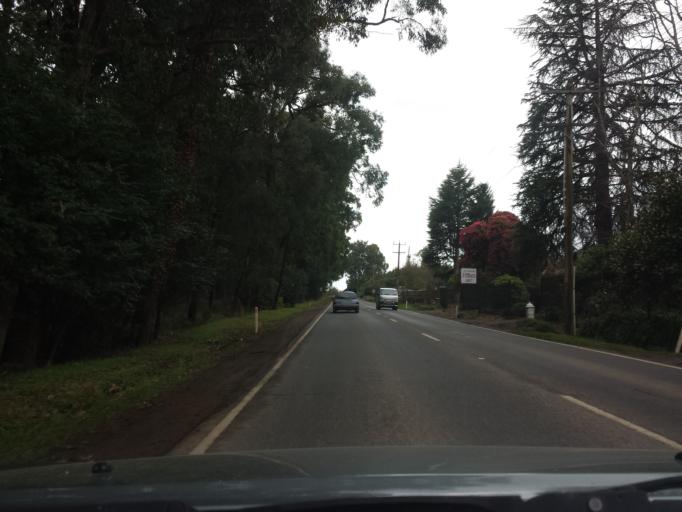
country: AU
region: Victoria
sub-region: Yarra Ranges
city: Monbulk
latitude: -37.8538
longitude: 145.4215
